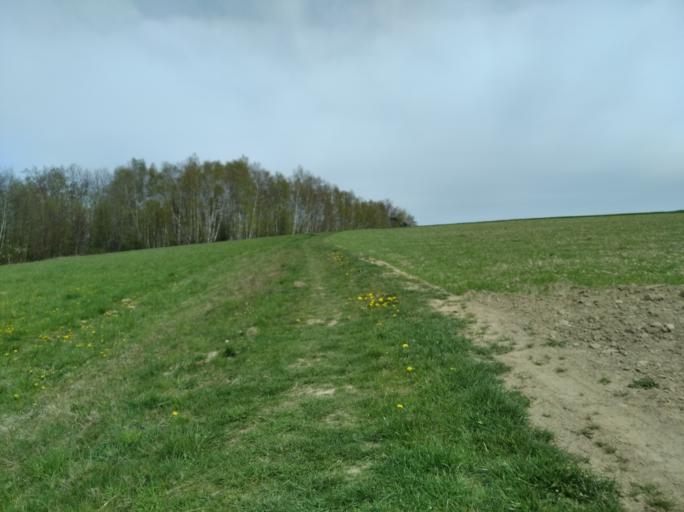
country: PL
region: Subcarpathian Voivodeship
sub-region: Powiat ropczycko-sedziszowski
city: Wielopole Skrzynskie
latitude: 49.9117
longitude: 21.6117
